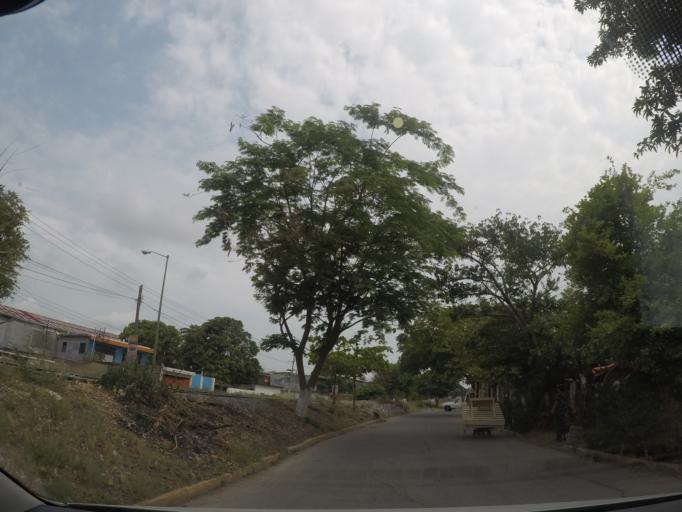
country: MX
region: Oaxaca
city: Juchitan de Zaragoza
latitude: 16.4439
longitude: -95.0211
